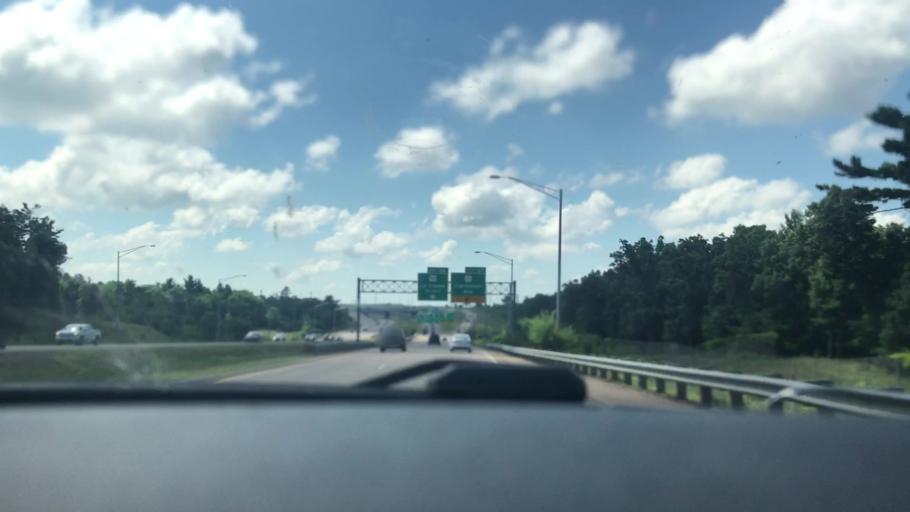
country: US
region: Wisconsin
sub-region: Eau Claire County
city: Altoona
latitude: 44.8030
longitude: -91.4559
